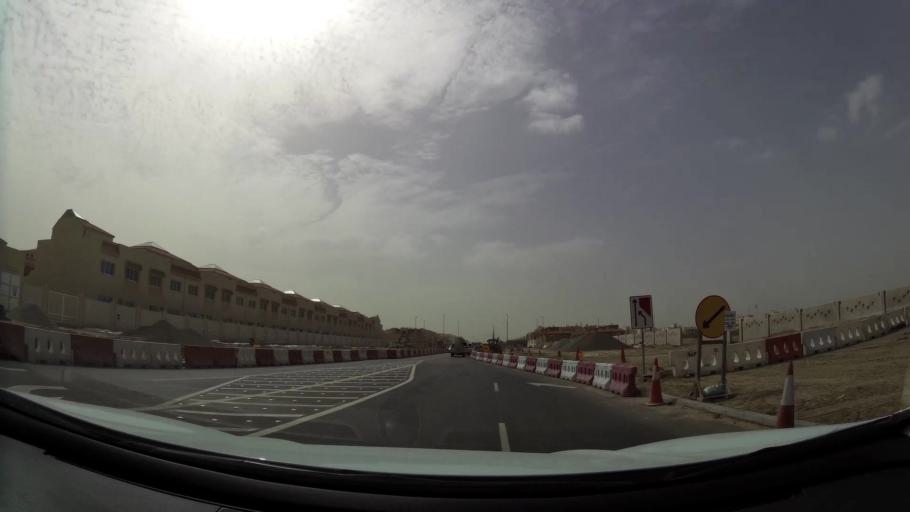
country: AE
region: Abu Dhabi
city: Abu Dhabi
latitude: 24.4036
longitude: 54.5716
